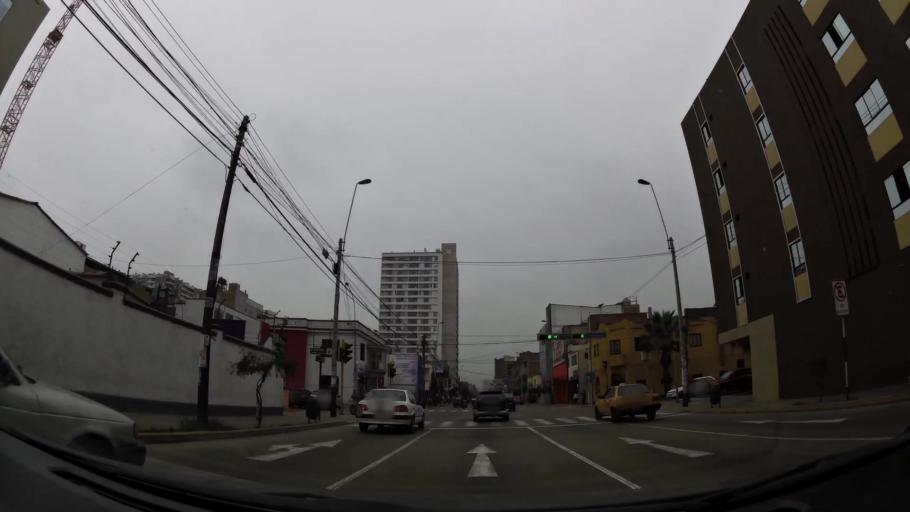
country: PE
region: Lima
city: Lima
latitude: -12.0808
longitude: -77.0339
